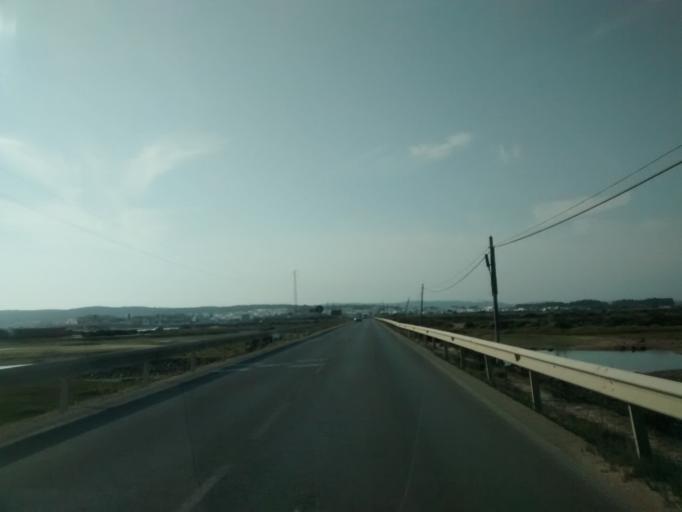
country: ES
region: Andalusia
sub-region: Provincia de Cadiz
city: Barbate de Franco
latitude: 36.1821
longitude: -5.9052
